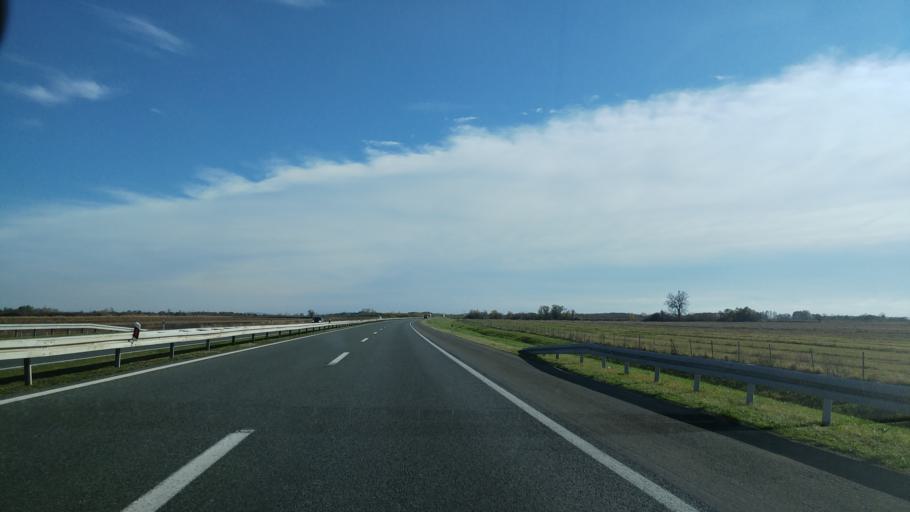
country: HR
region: Brodsko-Posavska
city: Okucani
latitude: 45.2601
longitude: 17.1649
